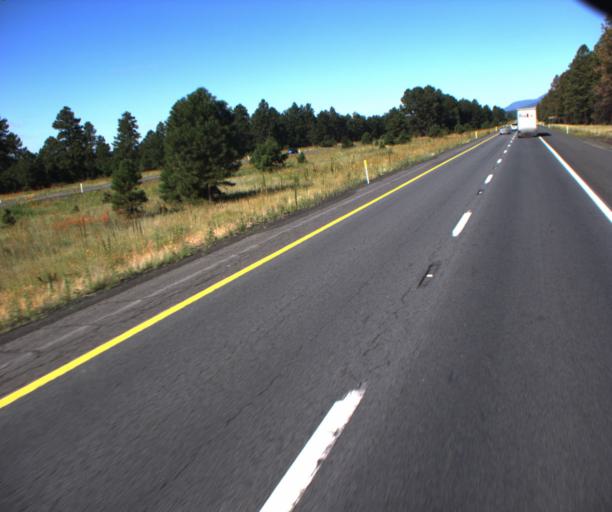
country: US
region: Arizona
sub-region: Coconino County
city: Parks
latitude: 35.2522
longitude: -111.9542
